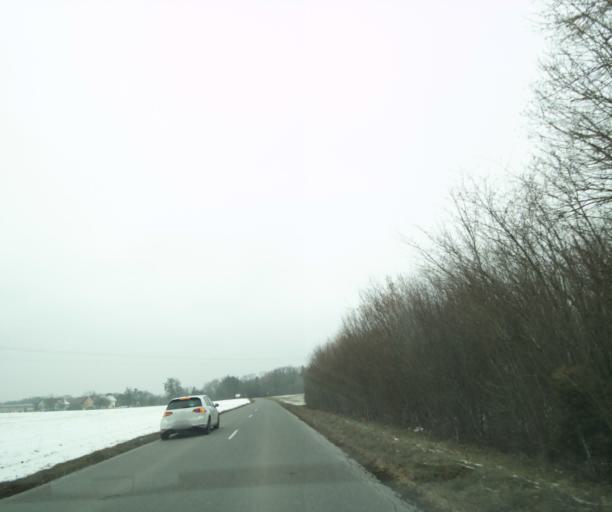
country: FR
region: Rhone-Alpes
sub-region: Departement de la Haute-Savoie
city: Contamine-sur-Arve
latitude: 46.1268
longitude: 6.3058
